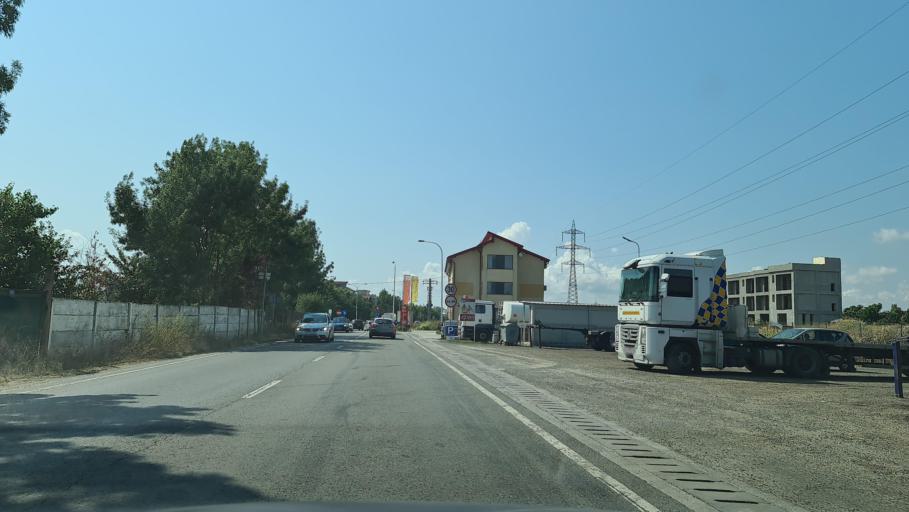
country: RO
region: Constanta
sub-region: Oras Eforie
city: Eforie Nord
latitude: 44.0836
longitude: 28.6397
